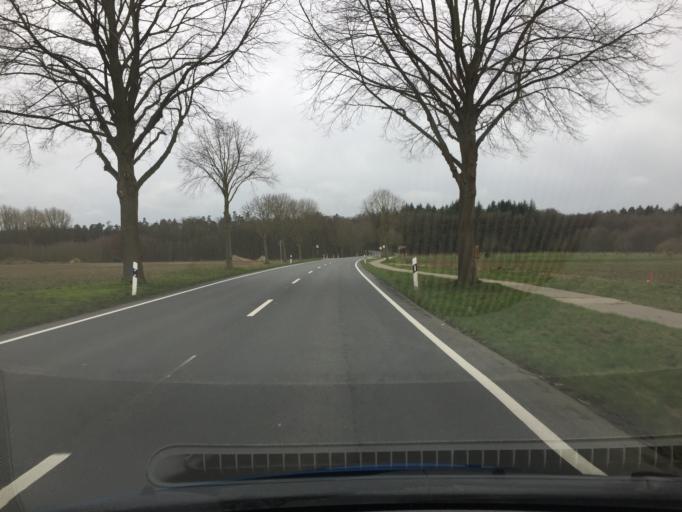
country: DE
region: Lower Saxony
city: Uelzen
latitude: 52.9802
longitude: 10.6153
